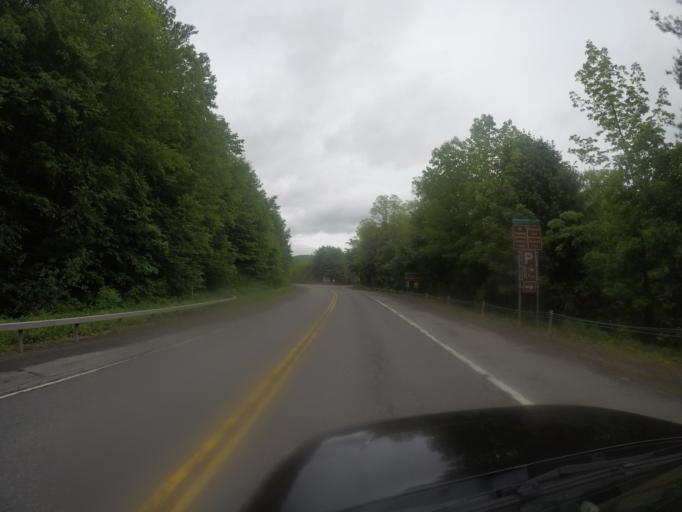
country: US
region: New York
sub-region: Ulster County
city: Shokan
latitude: 42.0786
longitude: -74.3085
